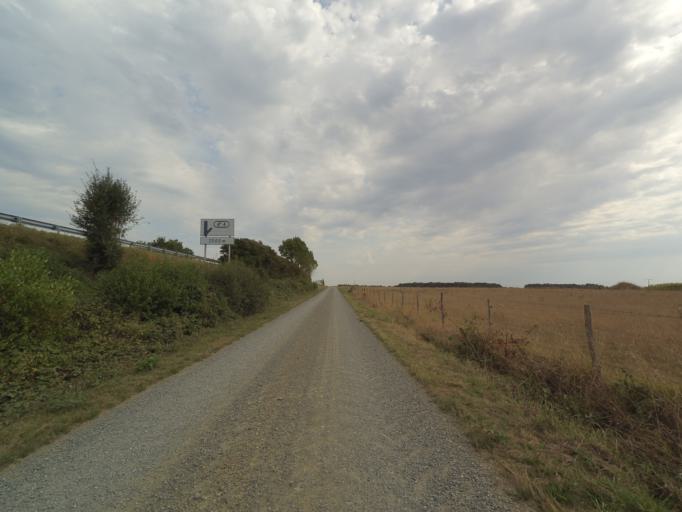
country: FR
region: Pays de la Loire
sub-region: Departement de la Vendee
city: Bouffere
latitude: 46.9811
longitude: -1.3762
